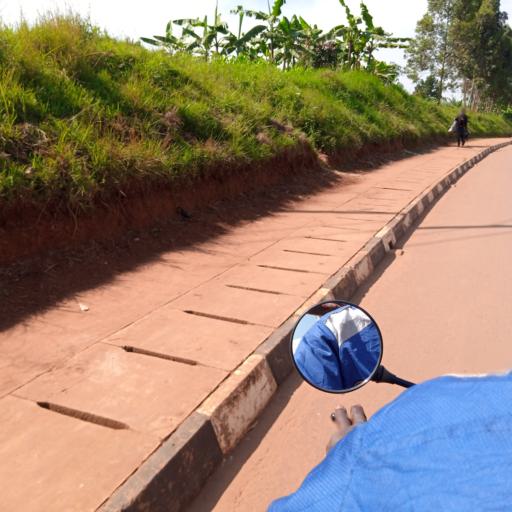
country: UG
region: Central Region
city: Masaka
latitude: -0.3440
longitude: 31.7311
